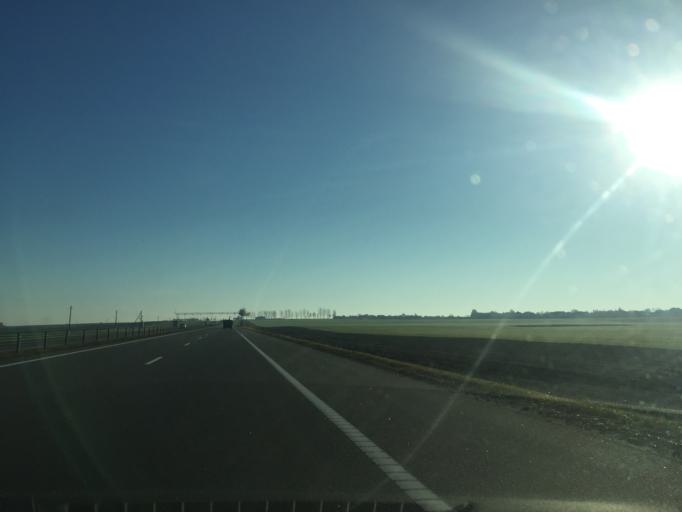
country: BY
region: Minsk
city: Luhavaya Slabada
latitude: 53.7614
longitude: 27.8958
